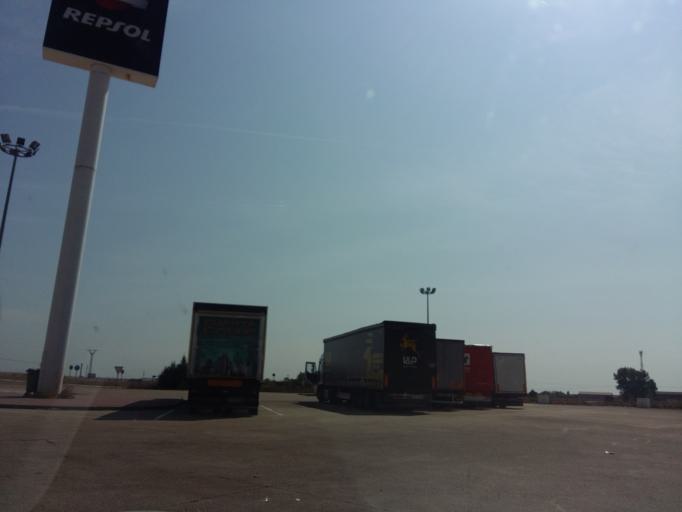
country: ES
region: Castille and Leon
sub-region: Provincia de Palencia
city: Villaherreros
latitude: 42.3914
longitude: -4.4745
